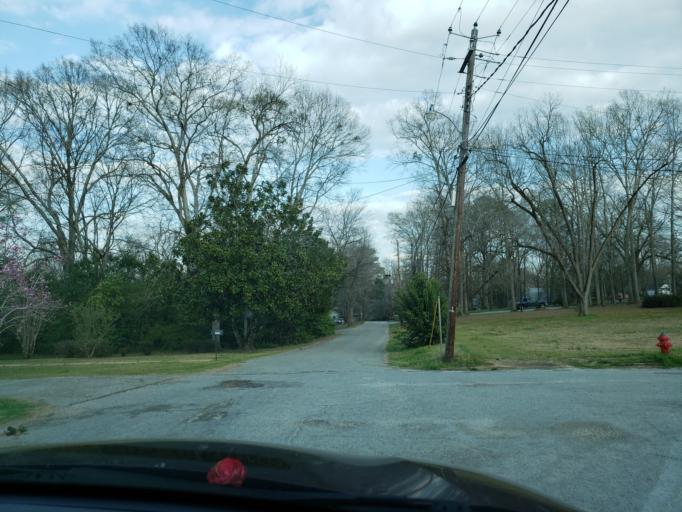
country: US
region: Alabama
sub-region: Hale County
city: Greensboro
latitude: 32.7077
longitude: -87.5940
